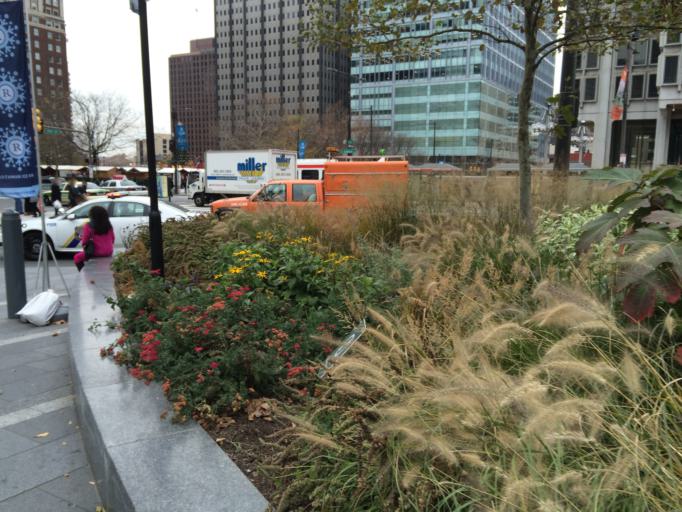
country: US
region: Pennsylvania
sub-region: Philadelphia County
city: Philadelphia
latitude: 39.9538
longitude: -75.1649
